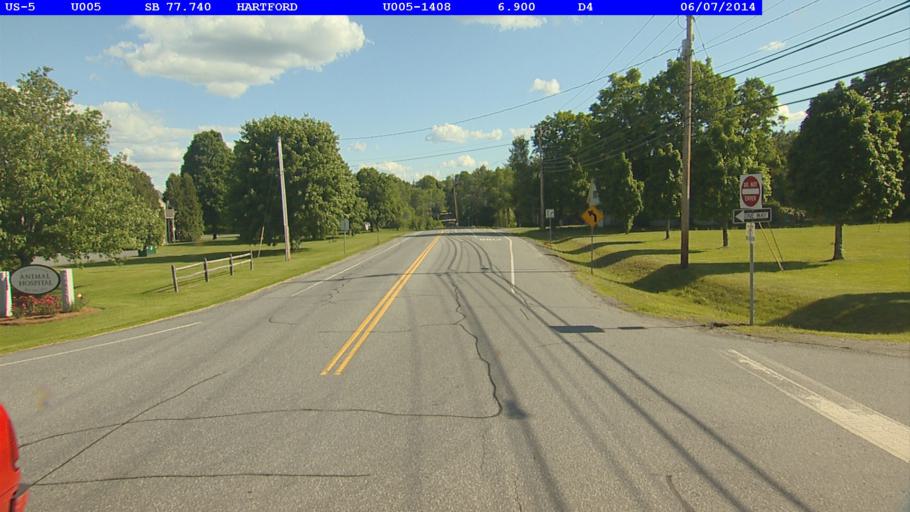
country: US
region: Vermont
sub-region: Windsor County
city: Wilder
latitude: 43.6870
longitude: -72.3209
